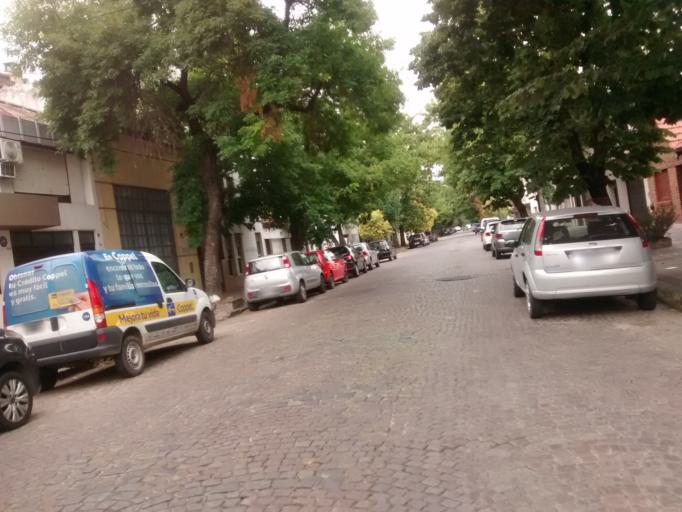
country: AR
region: Buenos Aires
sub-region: Partido de La Plata
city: La Plata
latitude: -34.9225
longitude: -57.9348
